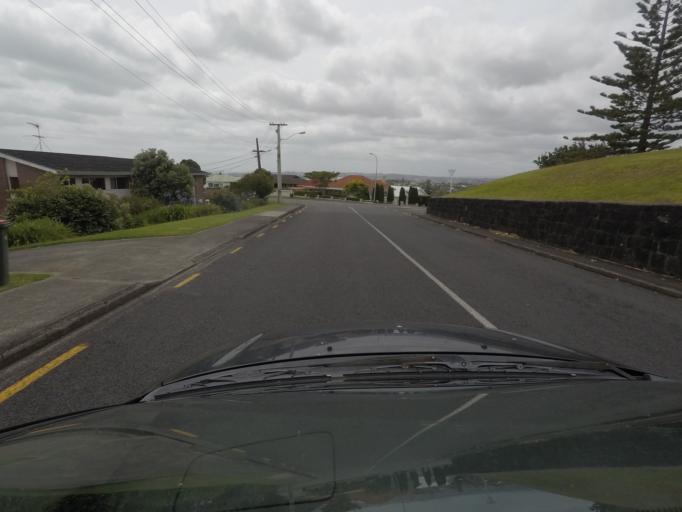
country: NZ
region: Auckland
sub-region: Auckland
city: Pakuranga
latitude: -36.8917
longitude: 174.9281
